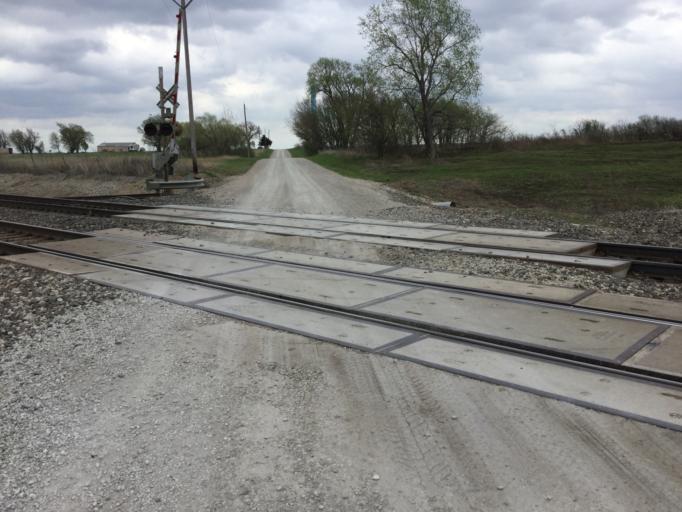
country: US
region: Kansas
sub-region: Osage County
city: Osage City
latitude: 38.4192
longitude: -95.8434
